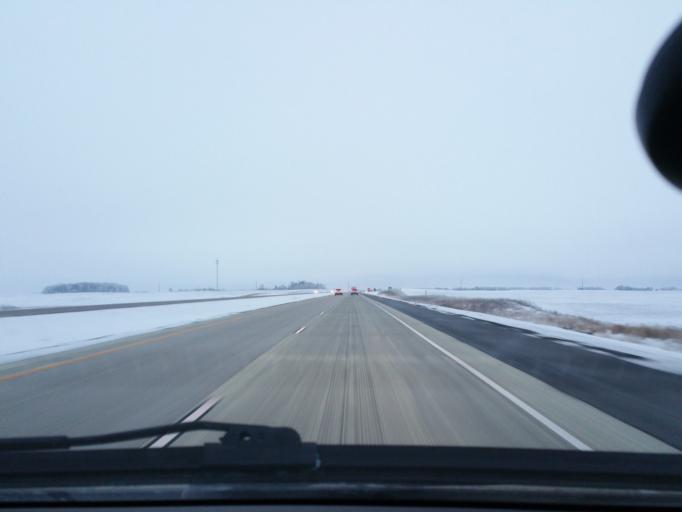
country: US
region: Minnesota
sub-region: Freeborn County
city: Albert Lea
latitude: 43.7227
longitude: -93.3206
